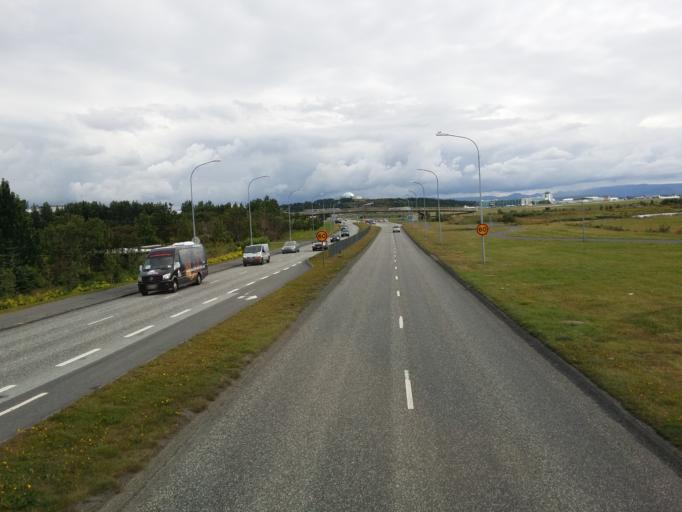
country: IS
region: Capital Region
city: Kopavogur
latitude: 64.1411
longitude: -21.9450
